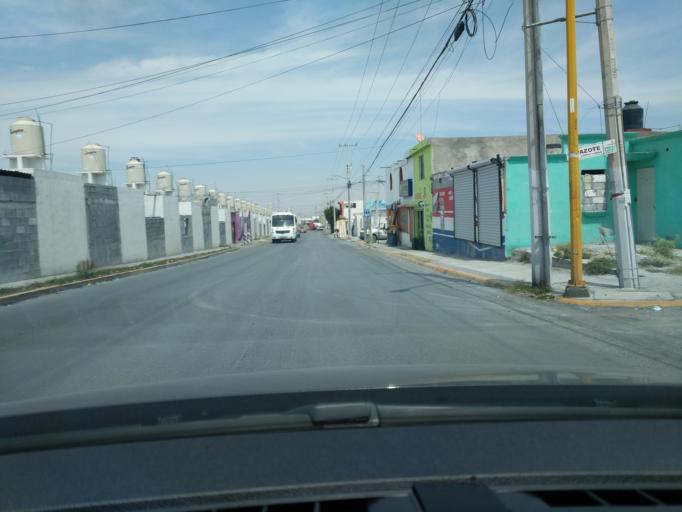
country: MX
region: Coahuila
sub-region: Arteaga
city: Arteaga
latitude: 25.4257
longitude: -100.9111
